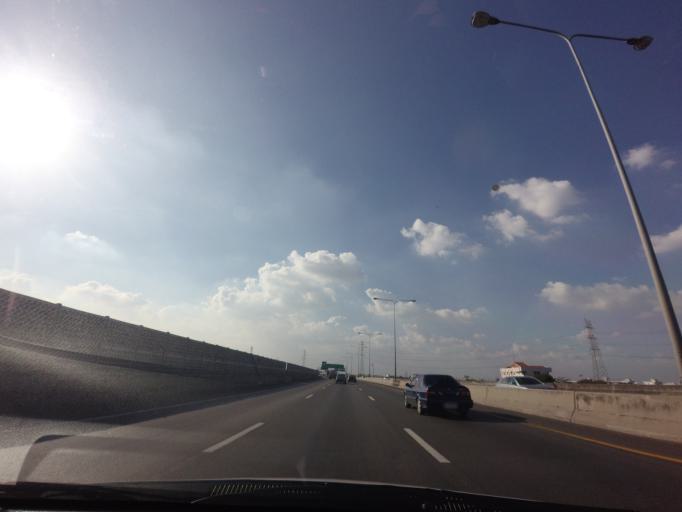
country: TH
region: Samut Prakan
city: Samut Prakan
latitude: 13.6214
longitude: 100.6069
